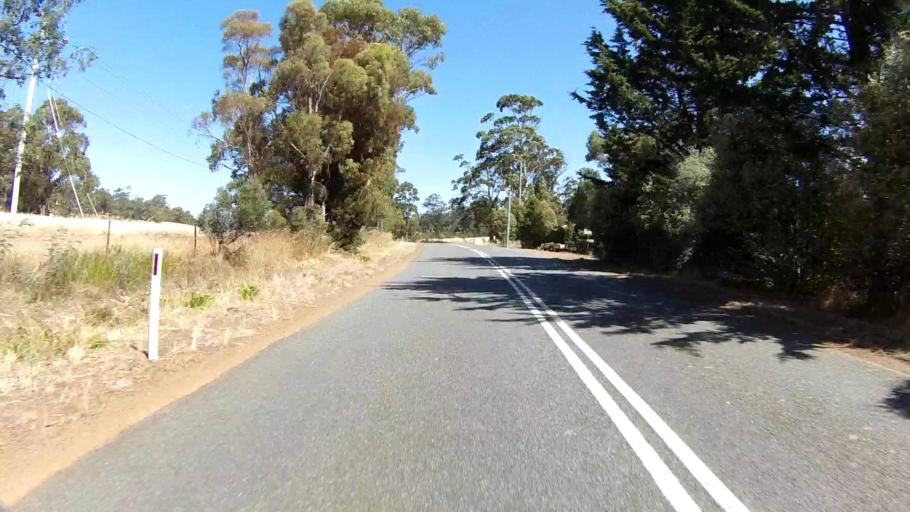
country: AU
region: Tasmania
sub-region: Sorell
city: Sorell
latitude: -42.3079
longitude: 147.9629
